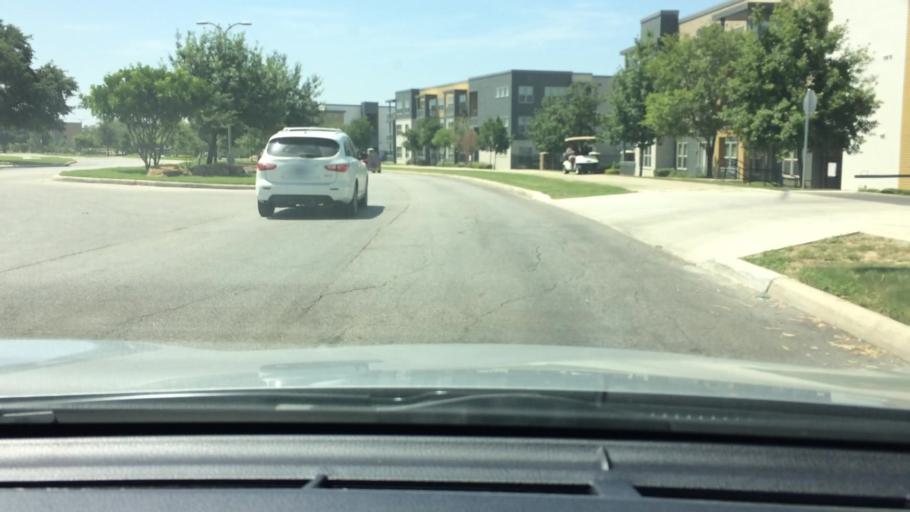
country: US
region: Texas
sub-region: Bexar County
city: San Antonio
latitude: 29.3498
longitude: -98.4486
